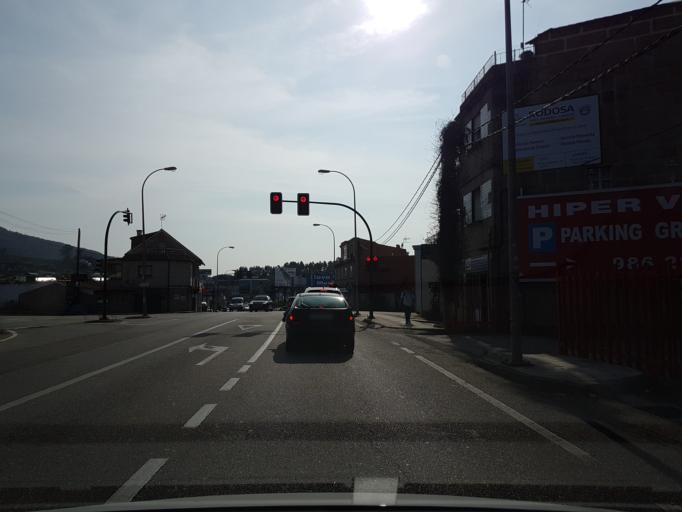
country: ES
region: Galicia
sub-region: Provincia de Pontevedra
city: Vigo
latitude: 42.1997
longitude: -8.7602
